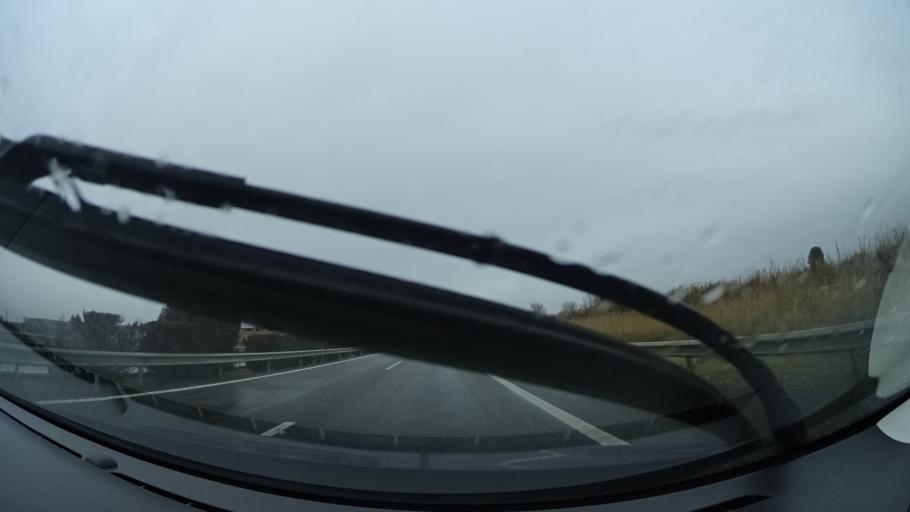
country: ES
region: Catalonia
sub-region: Provincia de Lleida
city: Lleida
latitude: 41.5714
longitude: 0.6223
